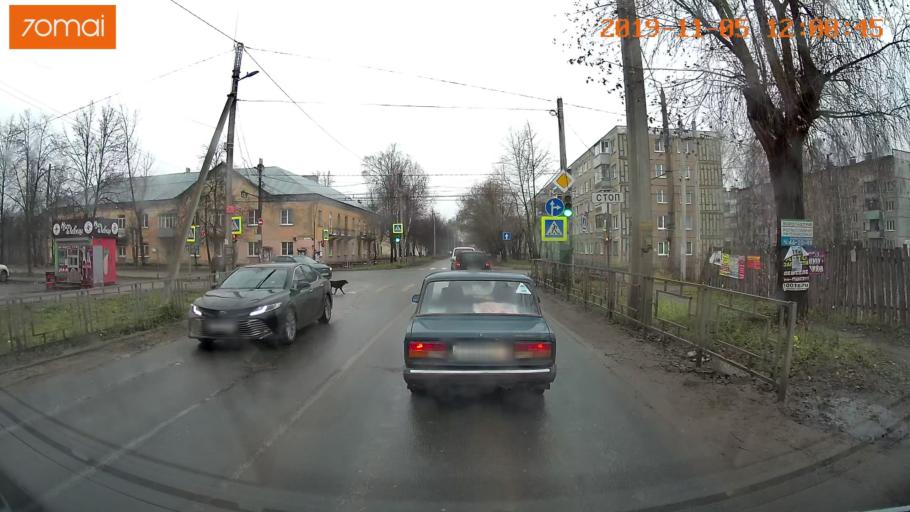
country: RU
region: Ivanovo
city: Kokhma
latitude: 56.9757
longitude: 41.0479
